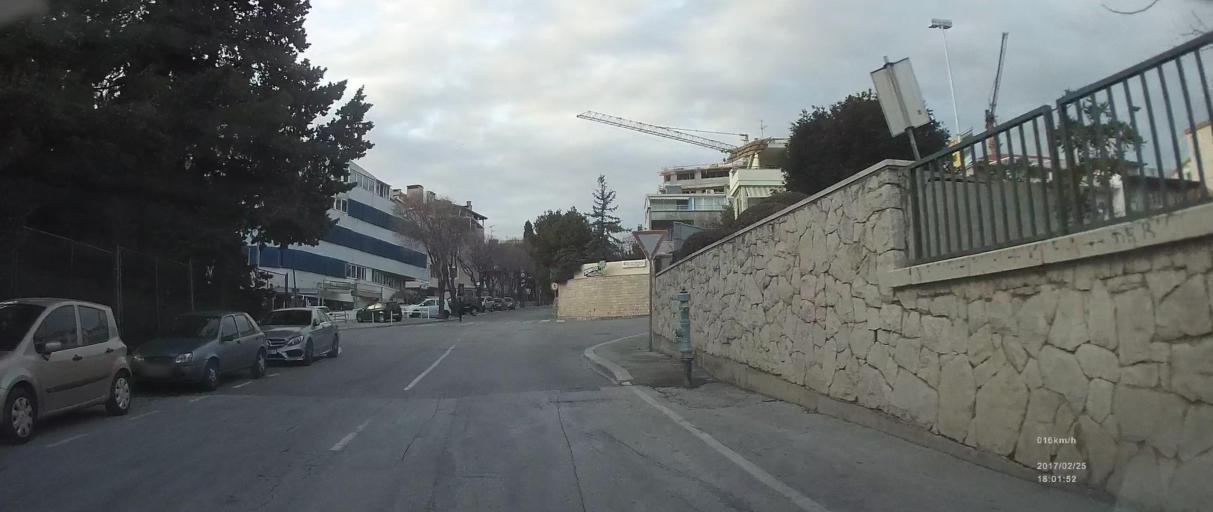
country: HR
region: Splitsko-Dalmatinska
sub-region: Grad Split
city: Split
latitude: 43.5014
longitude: 16.4574
